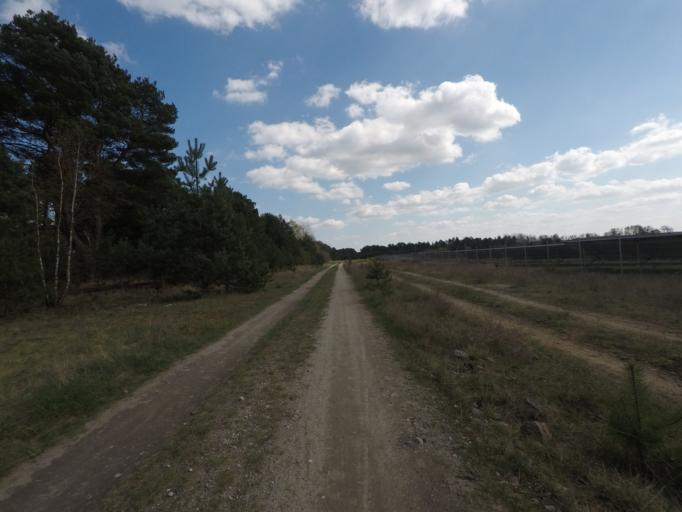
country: DE
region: Brandenburg
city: Melchow
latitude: 52.8339
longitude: 13.7073
